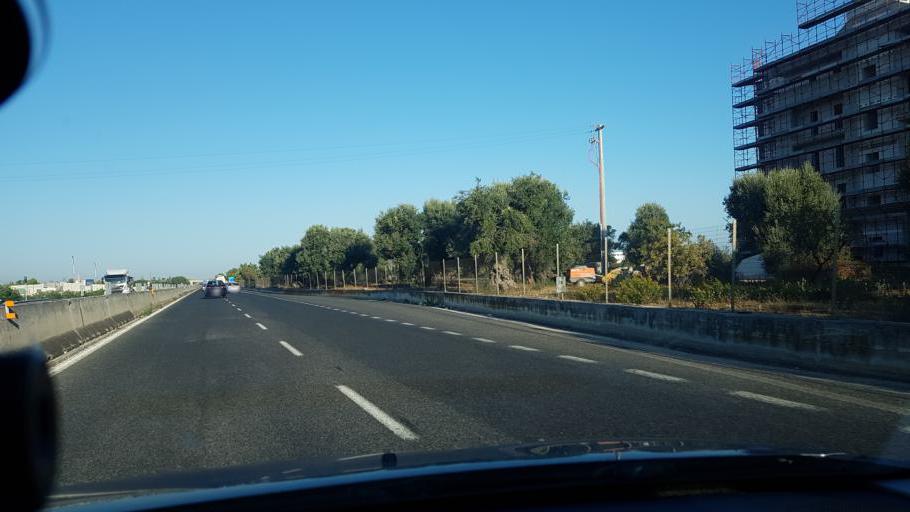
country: IT
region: Apulia
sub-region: Provincia di Bari
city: Monopoli
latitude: 40.9317
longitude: 17.3000
